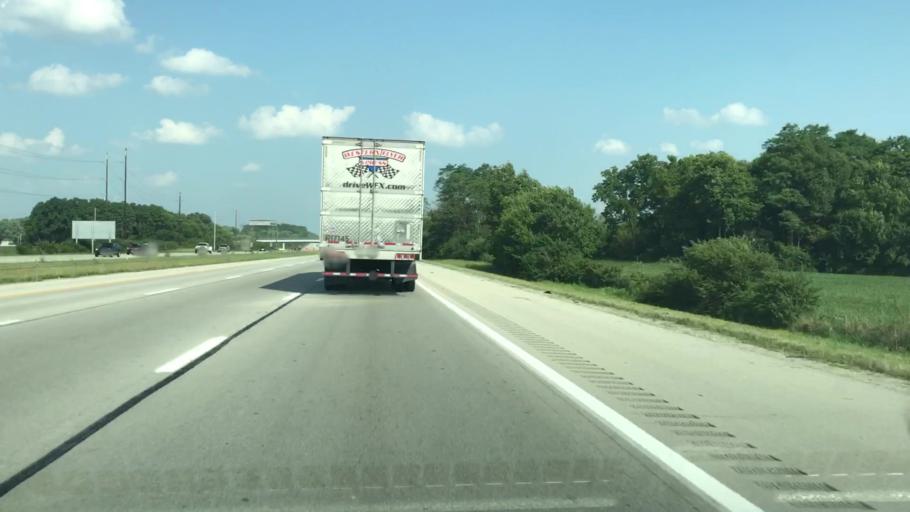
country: US
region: Ohio
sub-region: Clark County
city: Springfield
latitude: 39.8896
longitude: -83.7799
